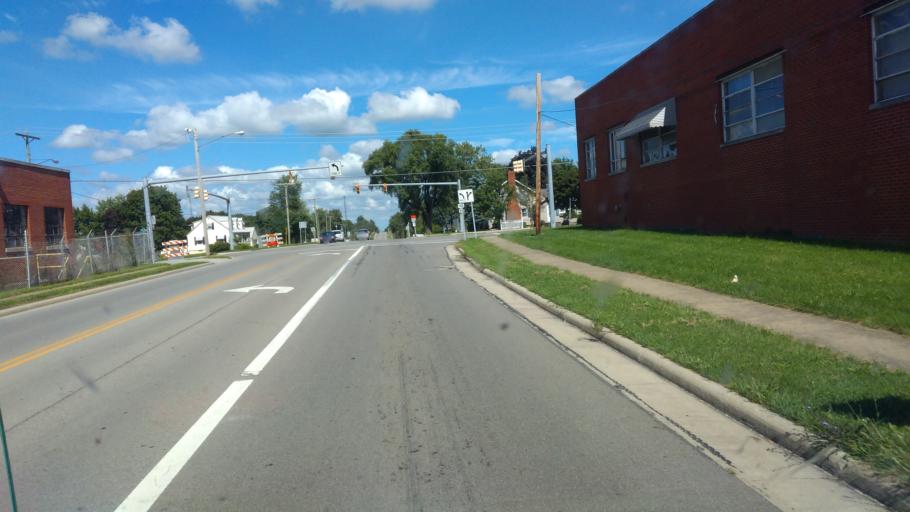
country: US
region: Ohio
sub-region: Huron County
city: Willard
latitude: 41.0524
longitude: -82.7160
